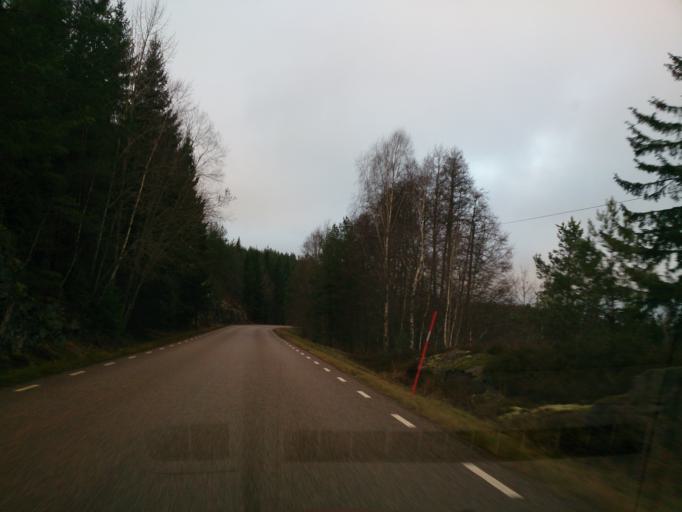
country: SE
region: OEstergoetland
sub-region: Atvidabergs Kommun
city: Atvidaberg
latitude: 58.2367
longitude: 16.0073
